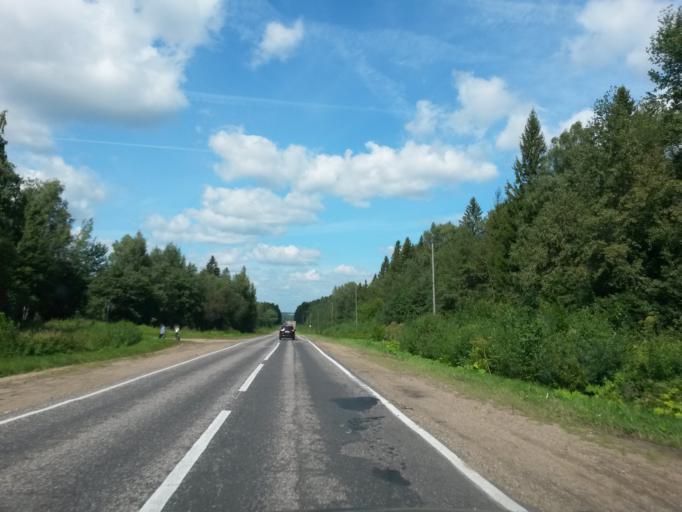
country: RU
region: Jaroslavl
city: Yaroslavl
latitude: 57.4940
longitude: 39.9007
